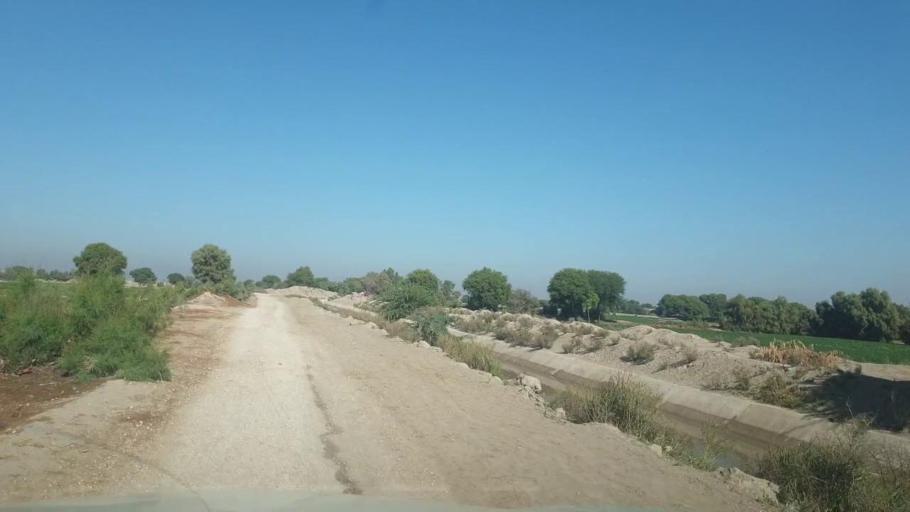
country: PK
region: Sindh
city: Bhan
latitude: 26.5582
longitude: 67.6302
